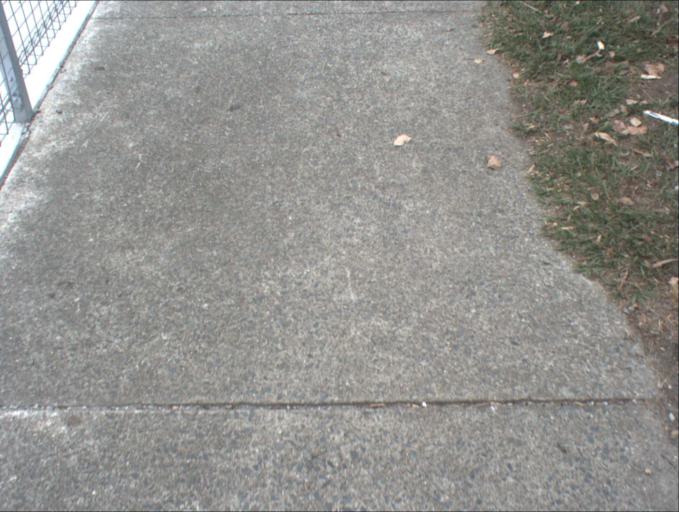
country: AU
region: Queensland
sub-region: Logan
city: Beenleigh
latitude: -27.7090
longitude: 153.1950
